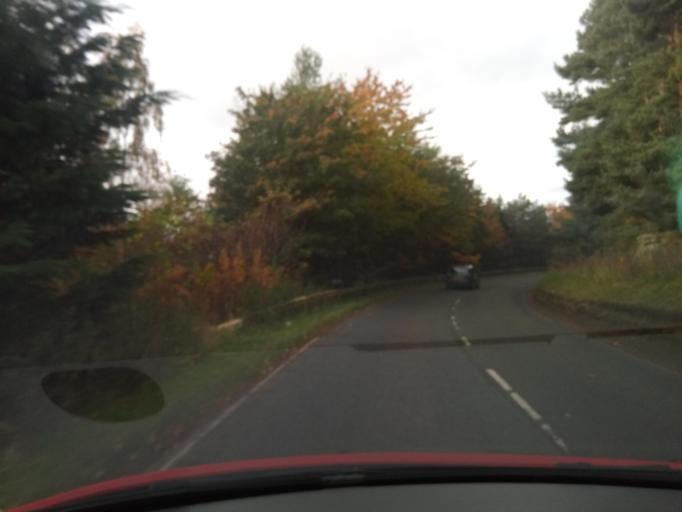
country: GB
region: Scotland
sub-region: The Scottish Borders
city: Peebles
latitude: 55.6425
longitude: -3.2430
